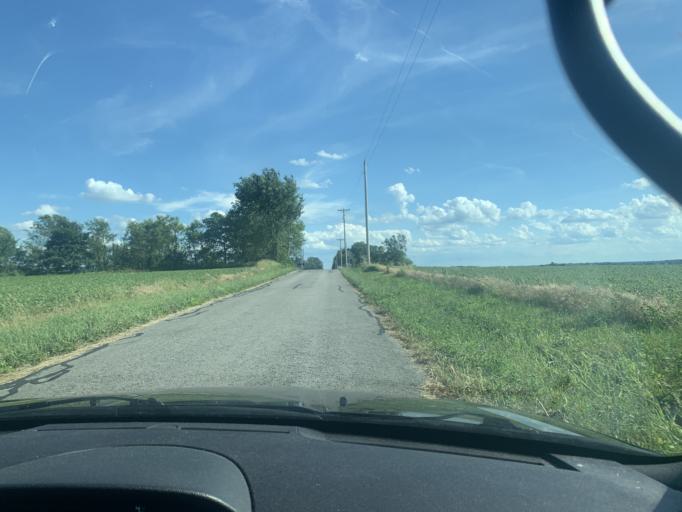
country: US
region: Ohio
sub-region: Logan County
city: De Graff
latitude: 40.3448
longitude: -83.8711
